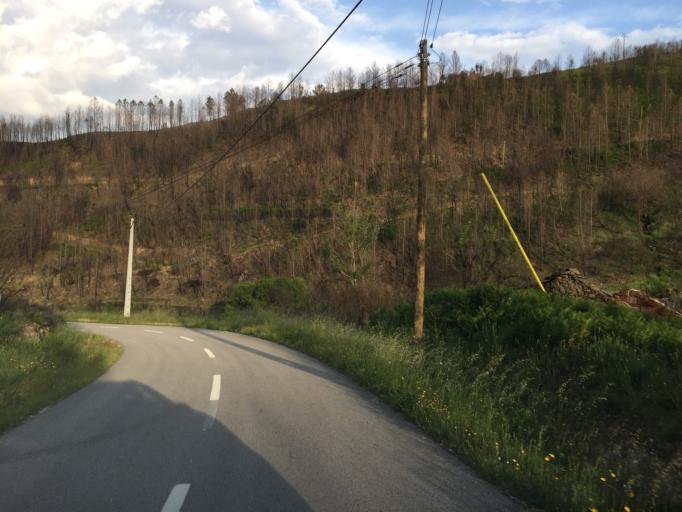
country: PT
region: Coimbra
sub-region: Arganil
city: Arganil
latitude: 40.1387
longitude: -8.0009
